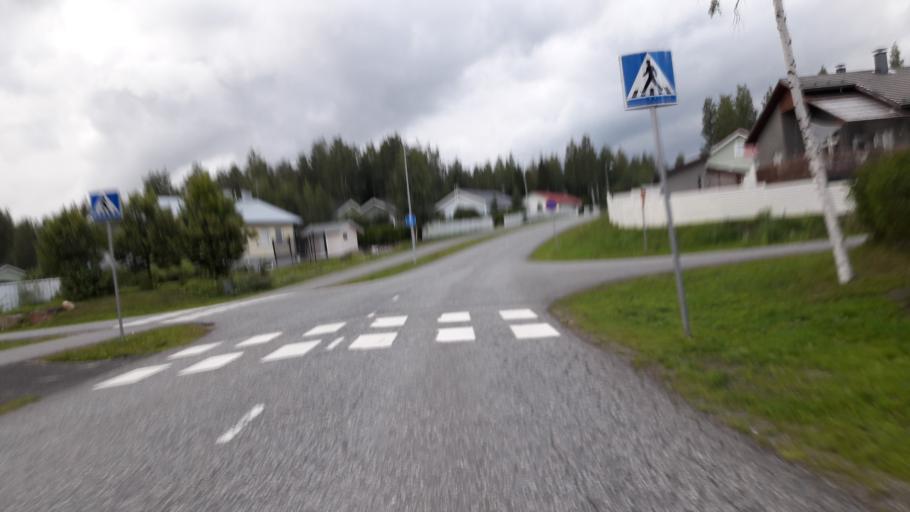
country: FI
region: North Karelia
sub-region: Joensuu
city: Joensuu
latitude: 62.5239
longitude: 29.8455
